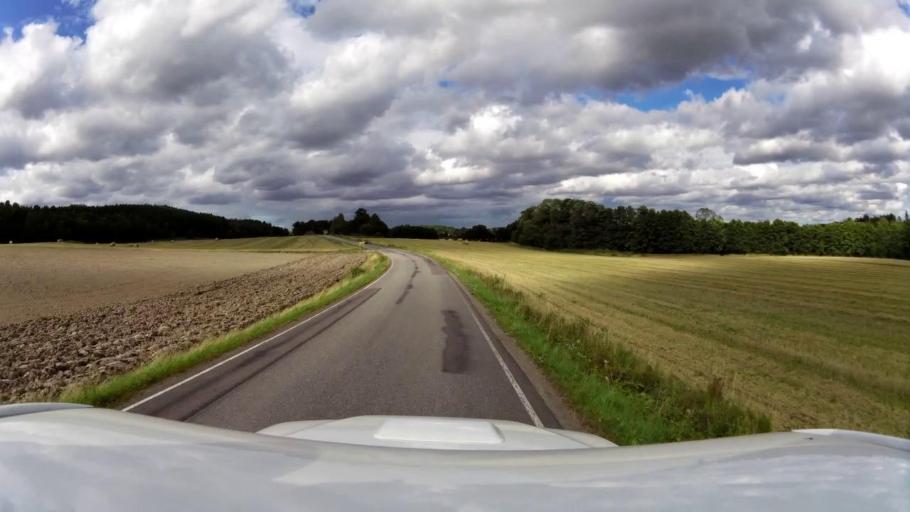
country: SE
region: OEstergoetland
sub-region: Linkopings Kommun
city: Sturefors
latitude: 58.3157
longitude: 15.7224
